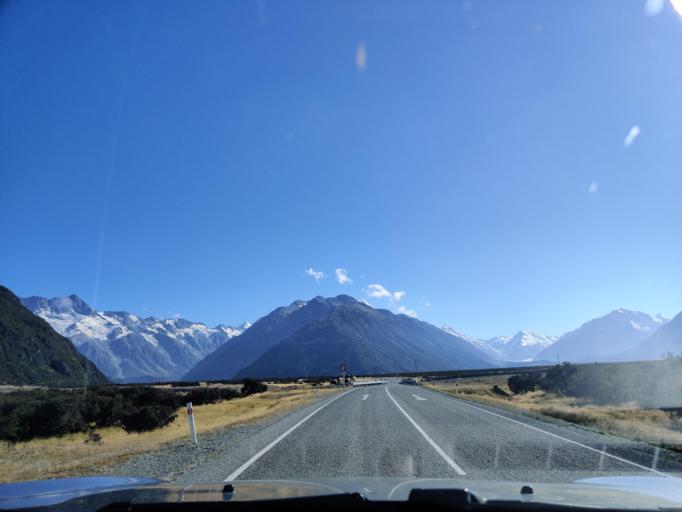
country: NZ
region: Canterbury
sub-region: Timaru District
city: Pleasant Point
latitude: -43.7699
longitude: 170.1228
